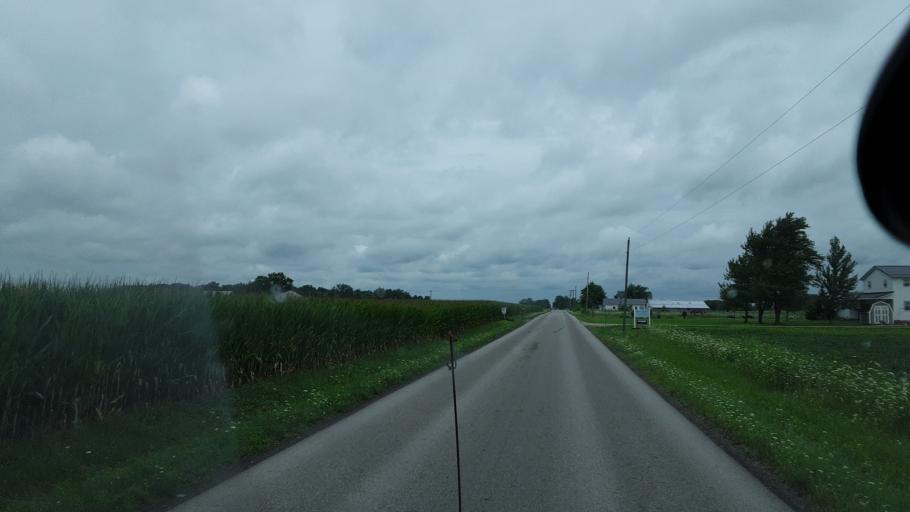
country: US
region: Indiana
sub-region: Adams County
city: Berne
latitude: 40.7256
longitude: -84.9944
